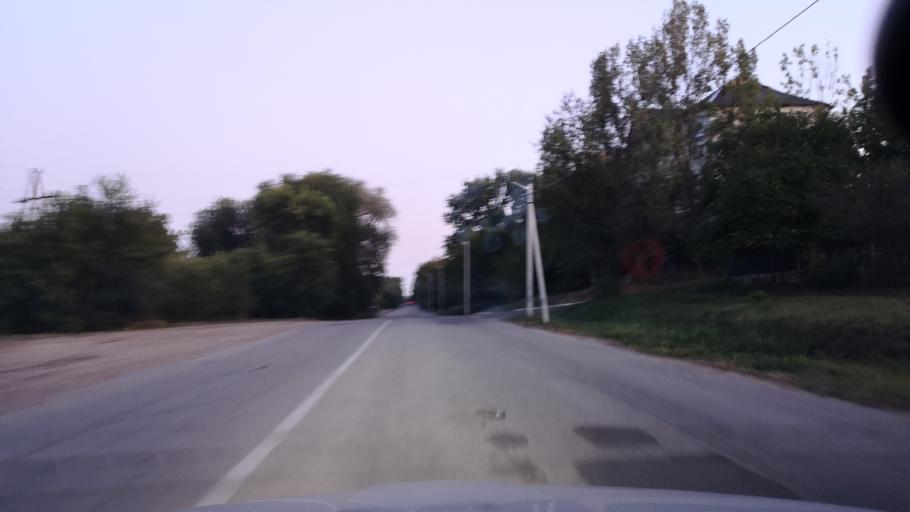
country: MD
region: Orhei
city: Orhei
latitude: 47.3993
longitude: 28.8197
